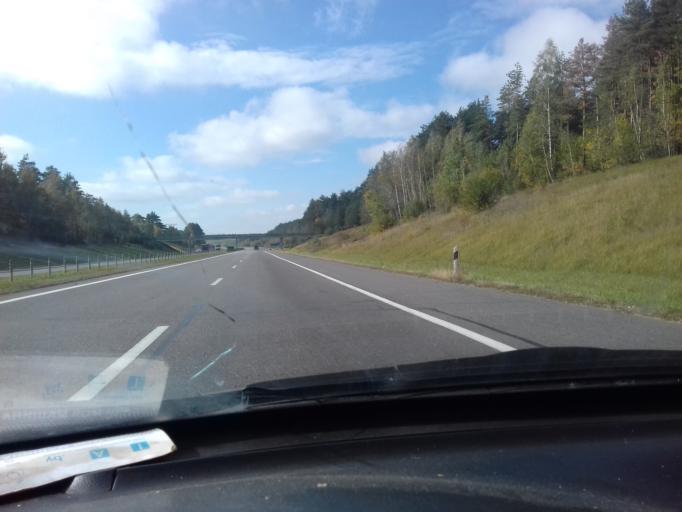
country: BY
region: Minsk
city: Pryvol'ny
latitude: 53.7952
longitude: 27.7462
